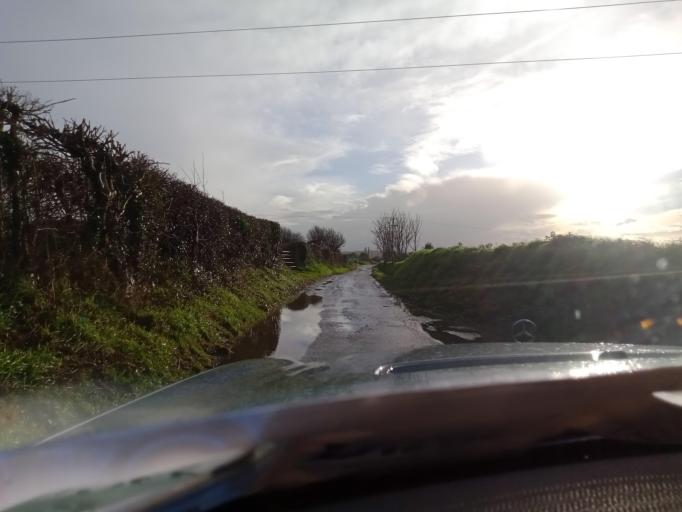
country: IE
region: Leinster
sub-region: Kilkenny
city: Mooncoin
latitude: 52.2797
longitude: -7.1926
